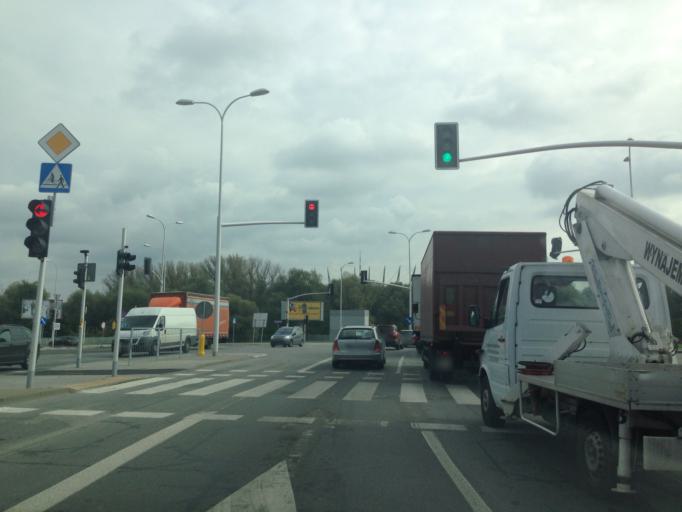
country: PL
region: Masovian Voivodeship
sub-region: Warszawa
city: Praga Polnoc
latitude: 52.2439
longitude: 21.0379
